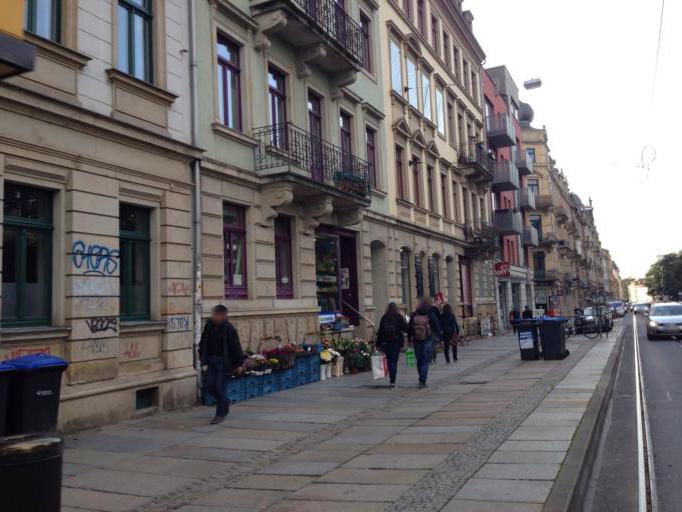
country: DE
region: Saxony
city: Albertstadt
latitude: 51.0699
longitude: 13.7555
